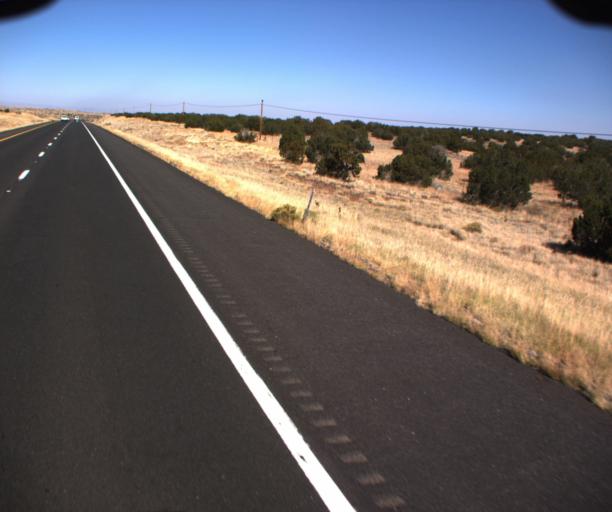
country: US
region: Arizona
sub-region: Coconino County
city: Flagstaff
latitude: 35.4856
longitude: -111.5556
